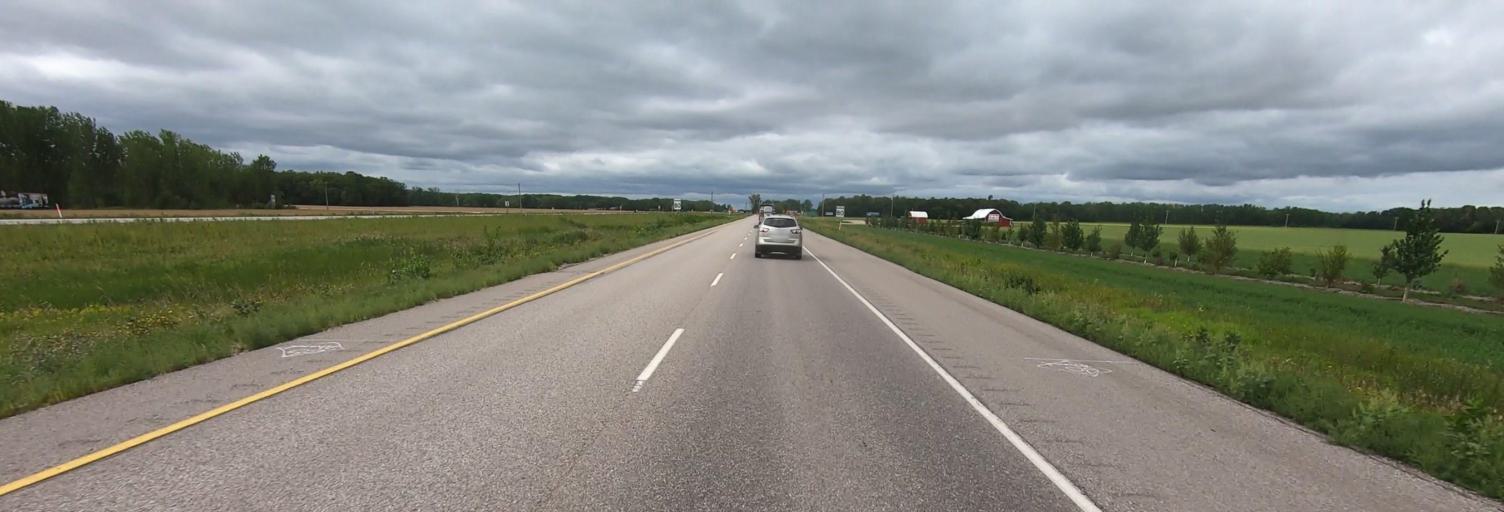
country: CA
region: Manitoba
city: Portage la Prairie
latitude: 49.9655
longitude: -98.0742
